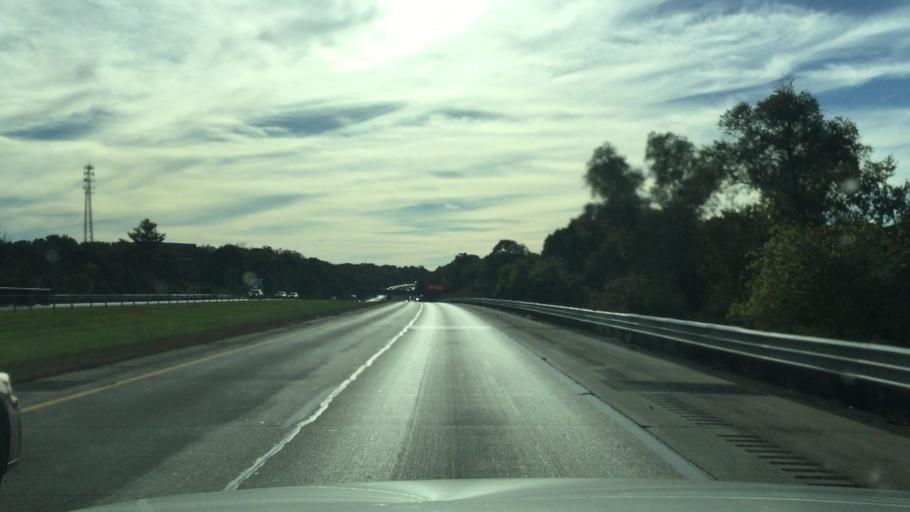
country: US
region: Michigan
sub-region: Calhoun County
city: Brownlee Park
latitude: 42.2947
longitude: -85.1018
